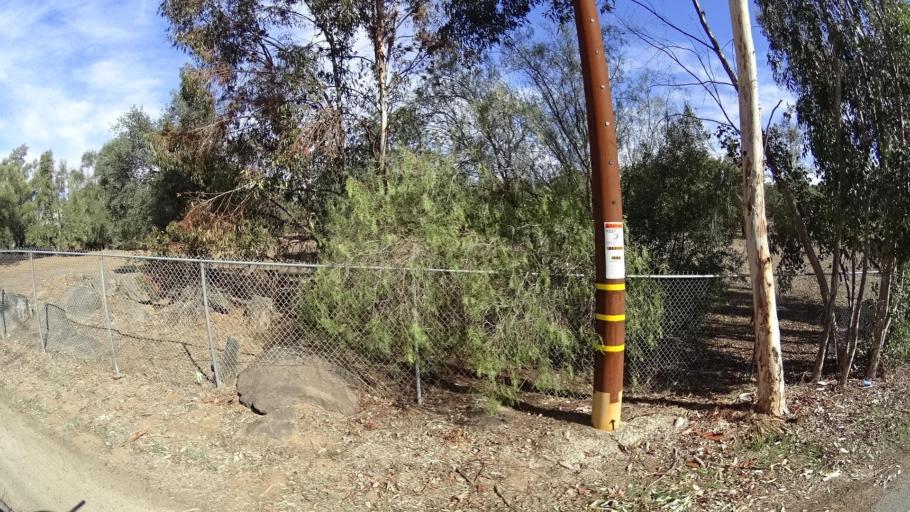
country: US
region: California
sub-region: San Diego County
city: Alpine
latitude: 32.8155
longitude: -116.7769
